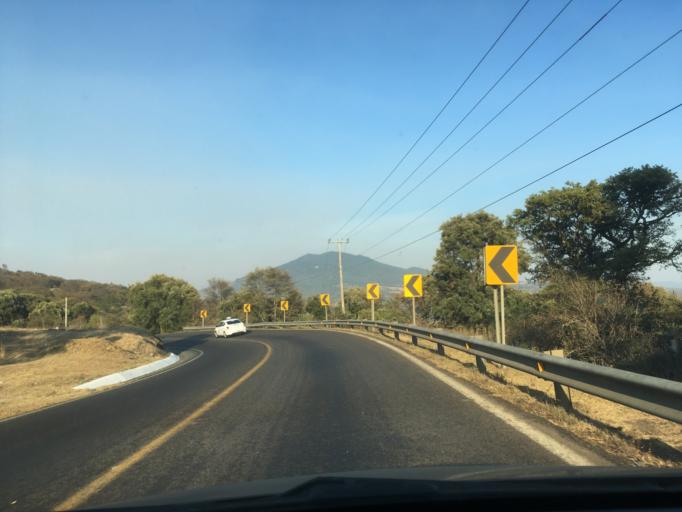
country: MX
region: Michoacan
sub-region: Morelia
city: Iratzio
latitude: 19.6298
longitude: -101.4443
